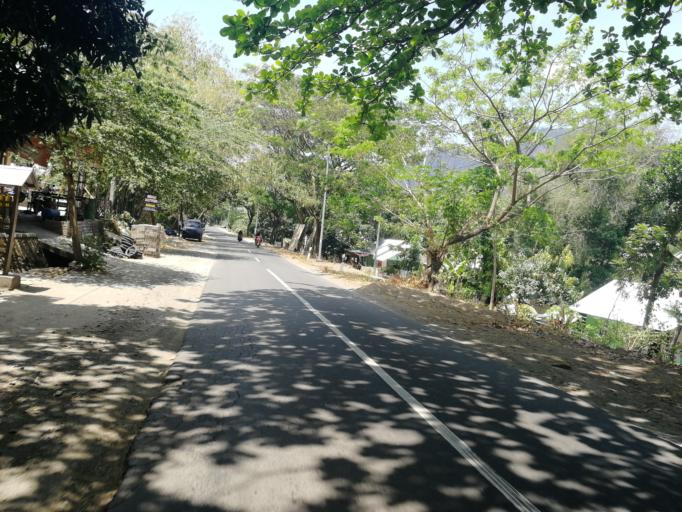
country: ID
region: West Nusa Tenggara
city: Karangsubagan
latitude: -8.4145
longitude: 116.0986
